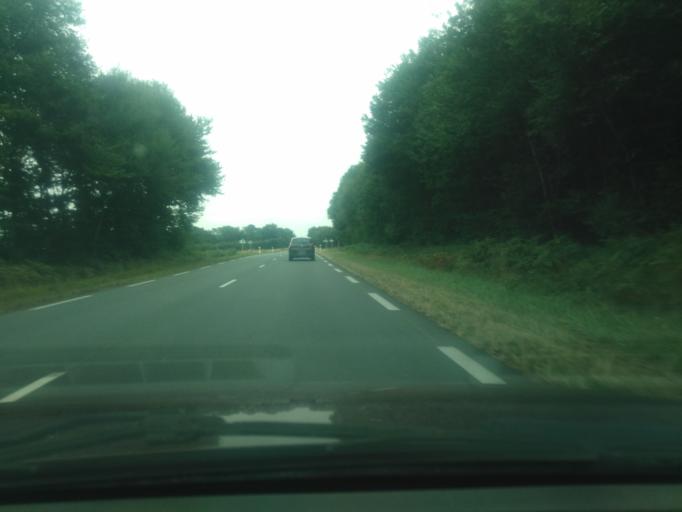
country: FR
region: Poitou-Charentes
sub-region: Departement de la Vienne
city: Chauvigny
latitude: 46.5731
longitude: 0.7429
